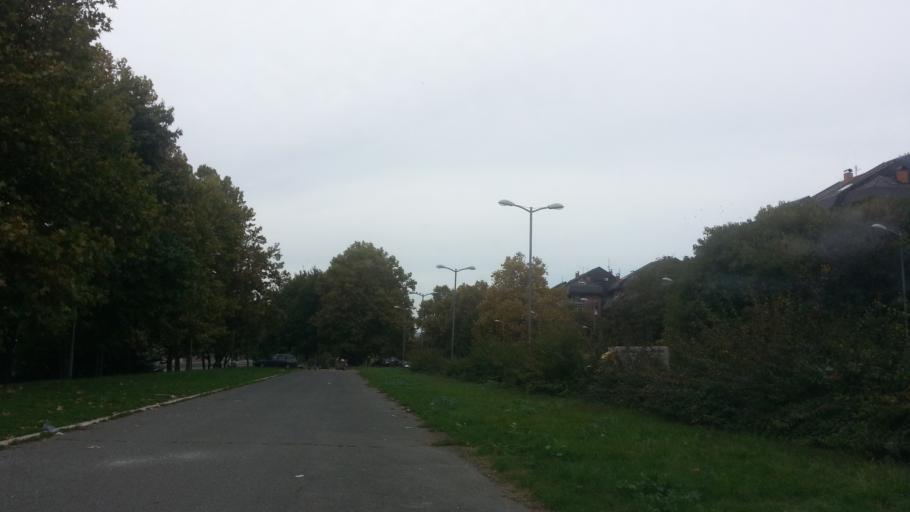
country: RS
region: Central Serbia
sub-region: Belgrade
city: Zemun
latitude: 44.8545
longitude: 20.3671
